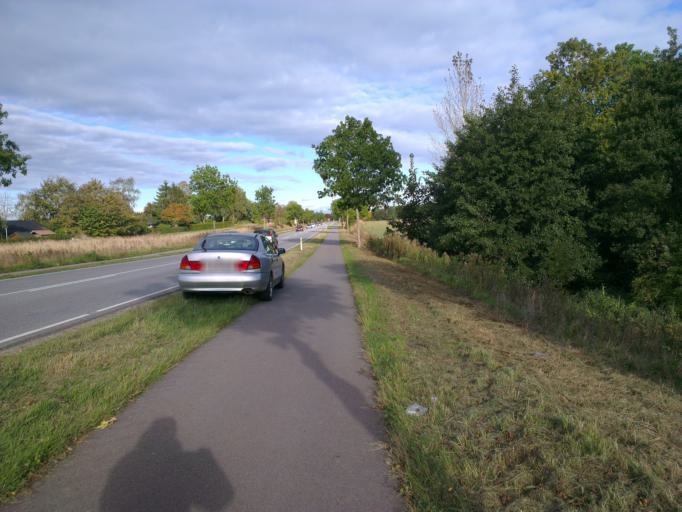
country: DK
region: Capital Region
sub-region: Frederikssund Kommune
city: Skibby
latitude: 55.7231
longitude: 11.9334
